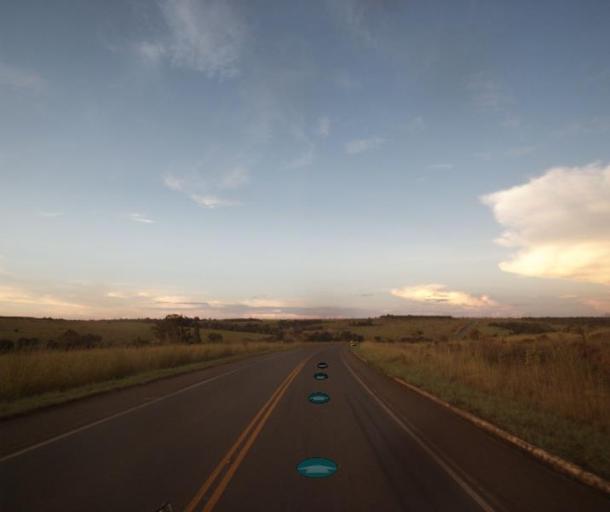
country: BR
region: Goias
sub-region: Pirenopolis
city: Pirenopolis
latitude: -16.0306
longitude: -48.8504
